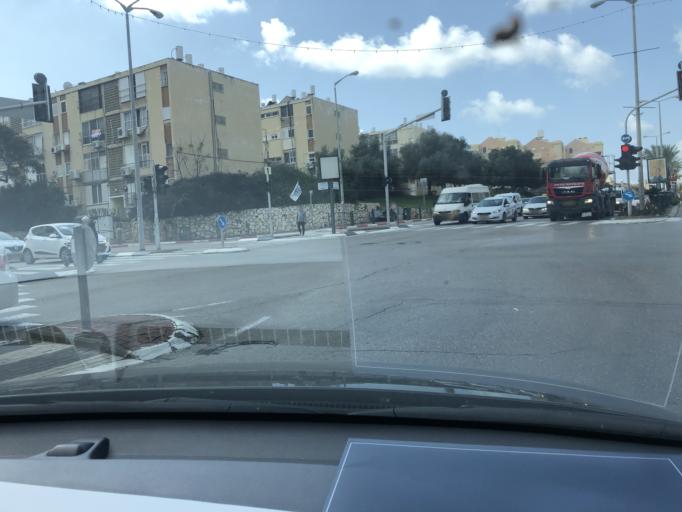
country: IL
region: Haifa
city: Hadera
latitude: 32.4410
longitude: 34.9151
